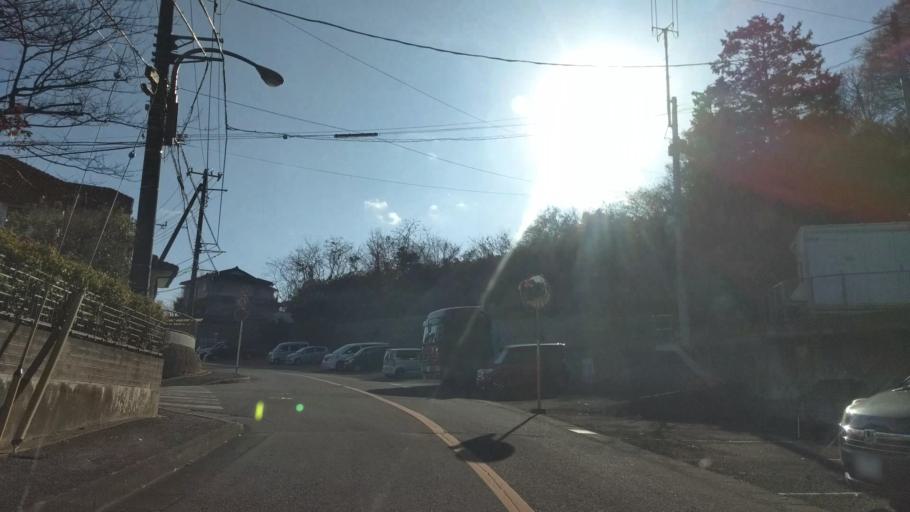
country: JP
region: Kanagawa
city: Hadano
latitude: 35.3672
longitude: 139.2516
